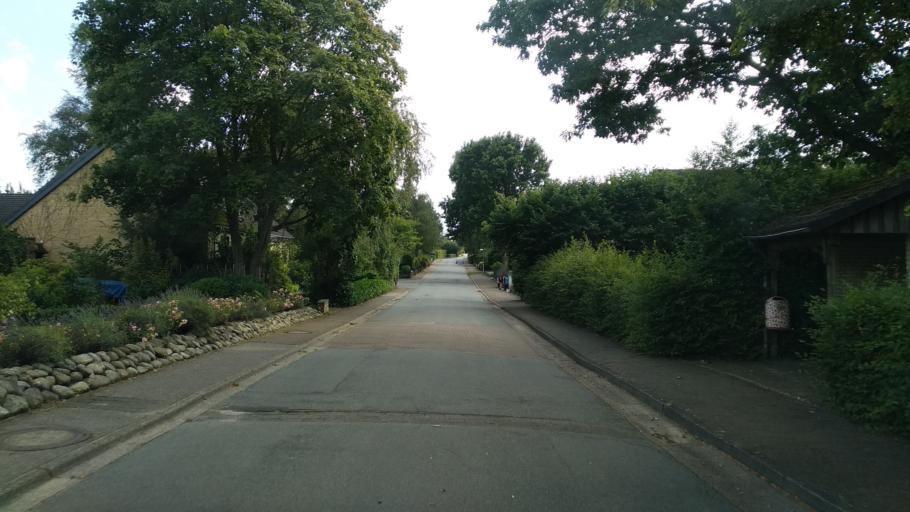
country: DE
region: Schleswig-Holstein
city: Neuberend
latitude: 54.5522
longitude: 9.5293
